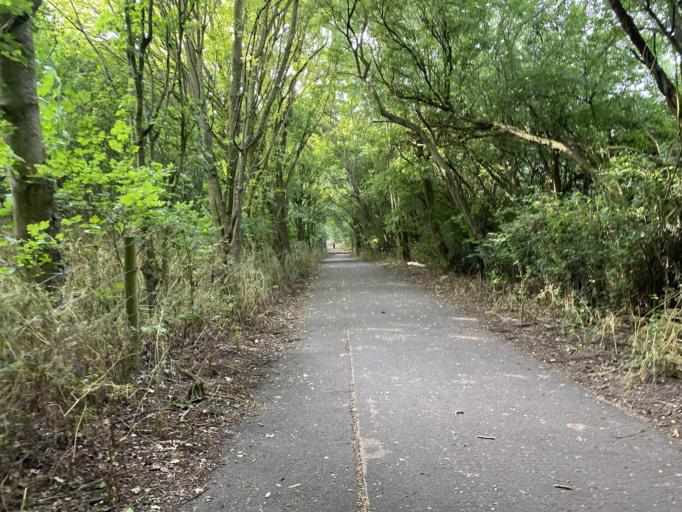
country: GB
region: England
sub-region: Suffolk
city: Haverhill
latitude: 52.0782
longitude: 0.4518
